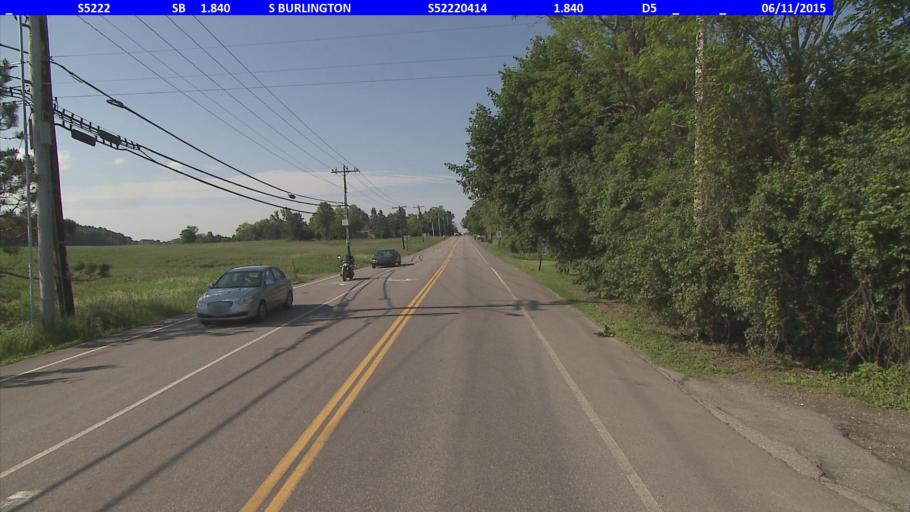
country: US
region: Vermont
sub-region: Chittenden County
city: South Burlington
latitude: 44.4429
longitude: -73.1890
